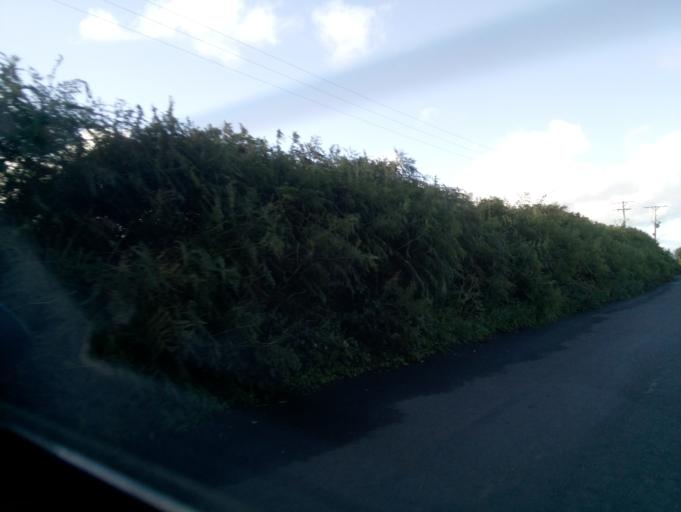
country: GB
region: England
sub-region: Devon
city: Dartmouth
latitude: 50.3307
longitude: -3.5999
